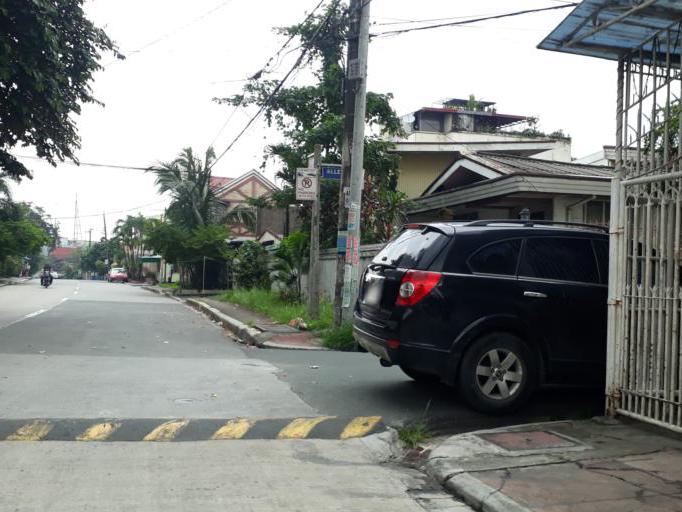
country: PH
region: Calabarzon
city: Bagong Pagasa
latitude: 14.6614
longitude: 121.0373
